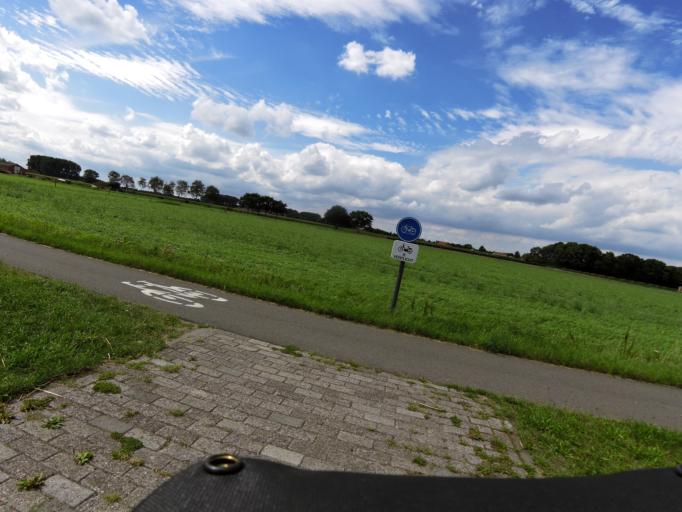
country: BE
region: Flanders
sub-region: Provincie Antwerpen
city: Hoogstraten
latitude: 51.4368
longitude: 4.7740
